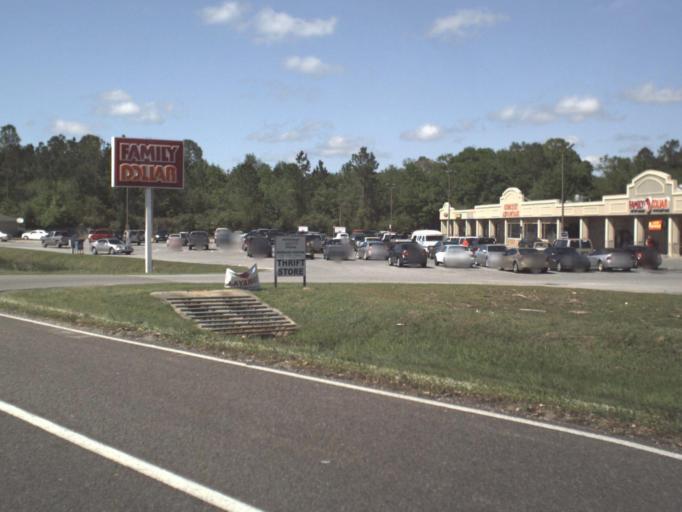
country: US
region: Florida
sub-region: Escambia County
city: Cantonment
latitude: 30.6195
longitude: -87.3255
